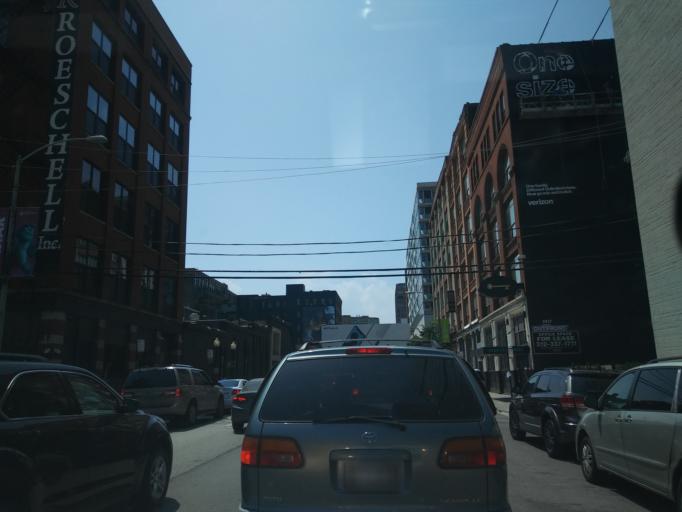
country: US
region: Illinois
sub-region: Cook County
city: Chicago
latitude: 41.8933
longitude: -87.6344
